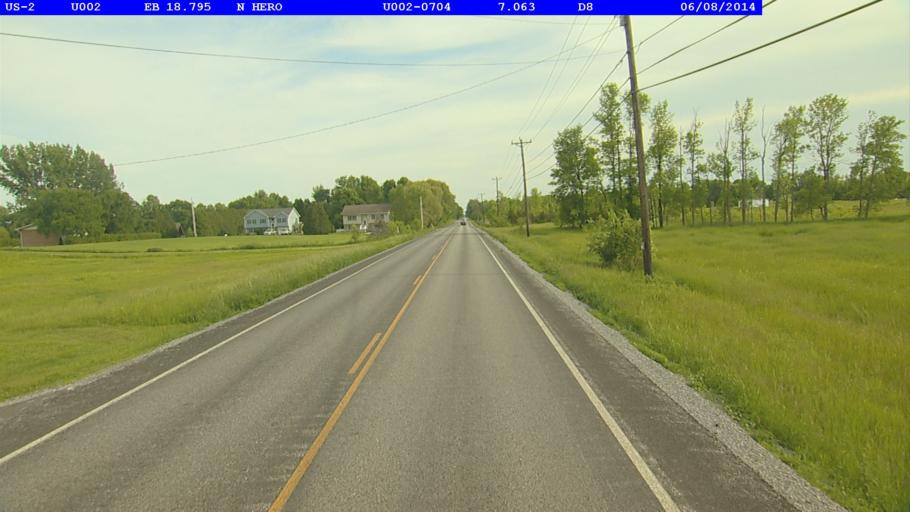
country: US
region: Vermont
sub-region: Grand Isle County
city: North Hero
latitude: 44.7978
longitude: -73.2923
